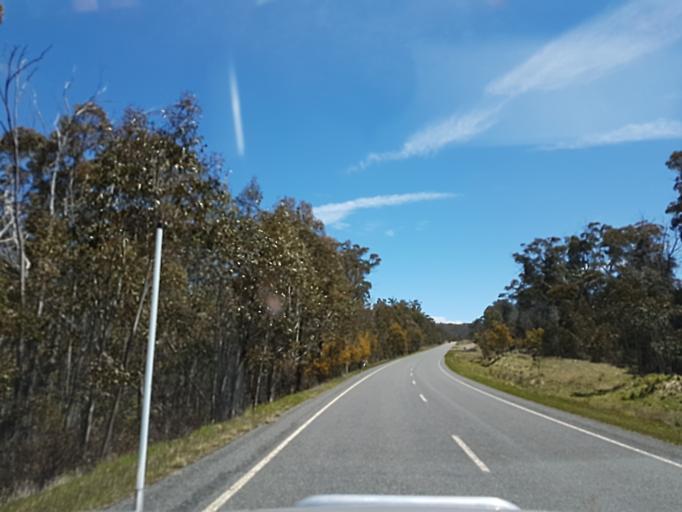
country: AU
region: Victoria
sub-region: Alpine
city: Mount Beauty
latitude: -37.0684
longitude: 147.3438
